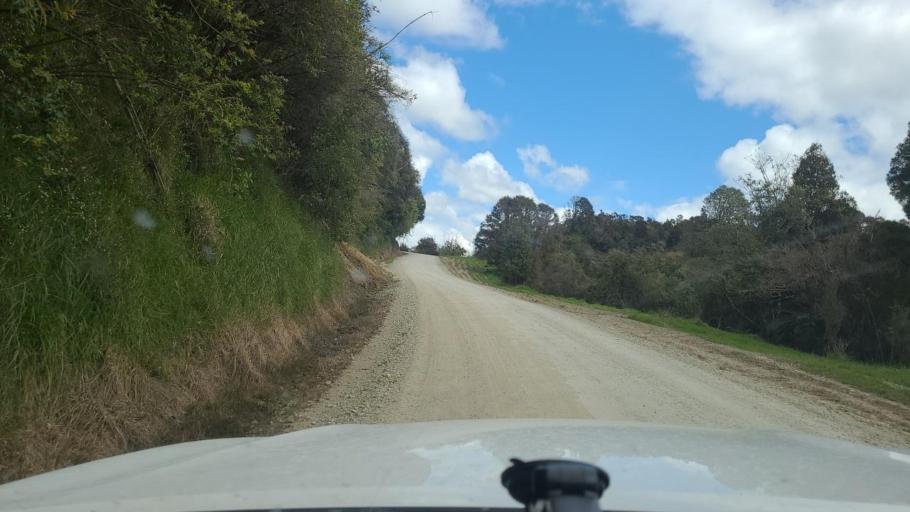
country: NZ
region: Gisborne
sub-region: Gisborne District
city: Gisborne
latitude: -38.8297
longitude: 177.7059
